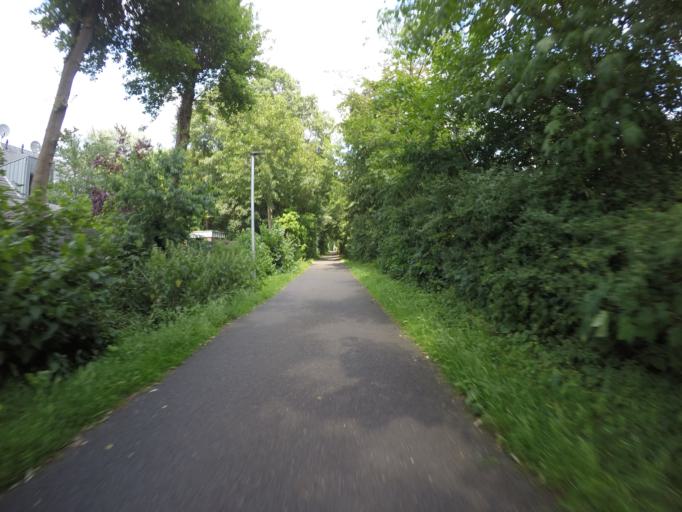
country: DE
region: North Rhine-Westphalia
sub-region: Regierungsbezirk Munster
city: Borken
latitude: 51.8479
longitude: 6.8442
